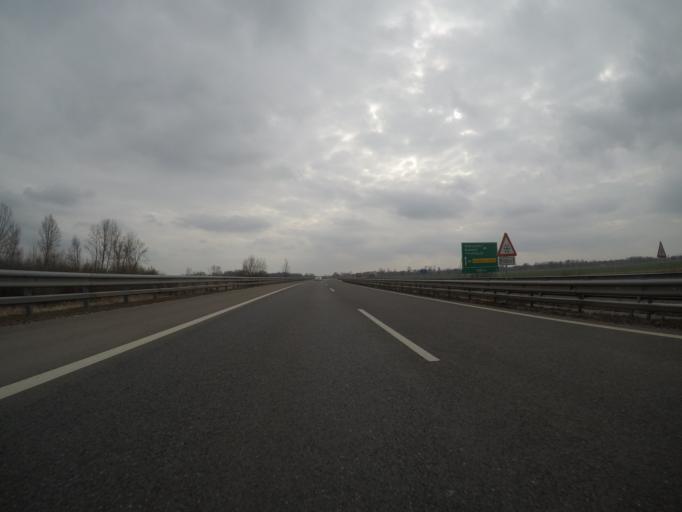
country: SI
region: Lendava-Lendva
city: Lendava
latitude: 46.5667
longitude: 16.4442
